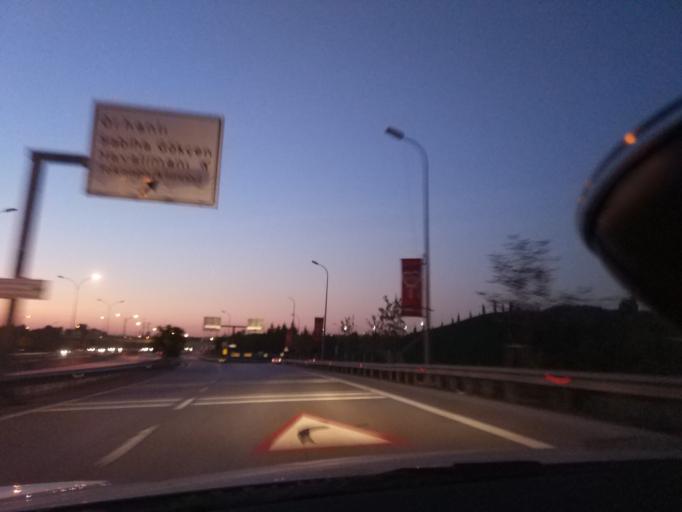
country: TR
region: Istanbul
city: Pendik
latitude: 40.9174
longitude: 29.3221
